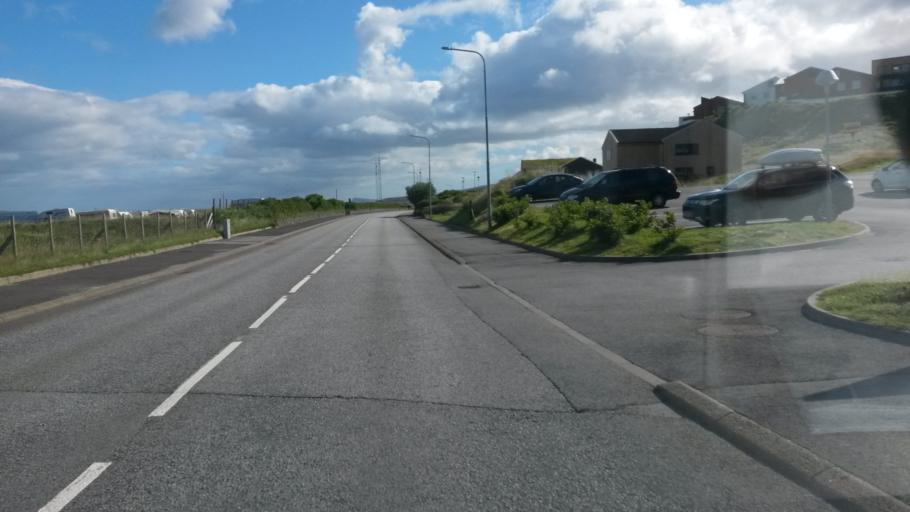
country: FO
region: Streymoy
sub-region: Torshavn
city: Torshavn
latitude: 62.0182
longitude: -6.7562
